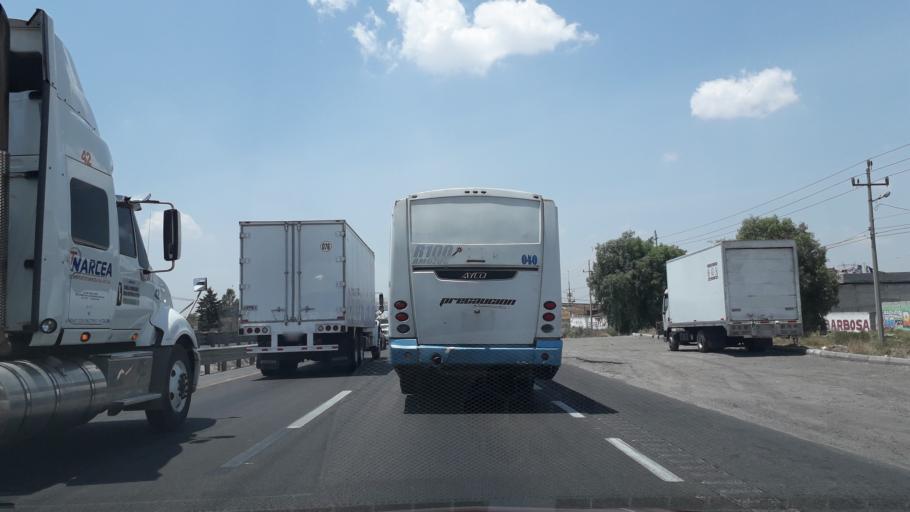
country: MX
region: Puebla
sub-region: Amozoc
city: Casa Blanca
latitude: 19.0711
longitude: -98.1323
